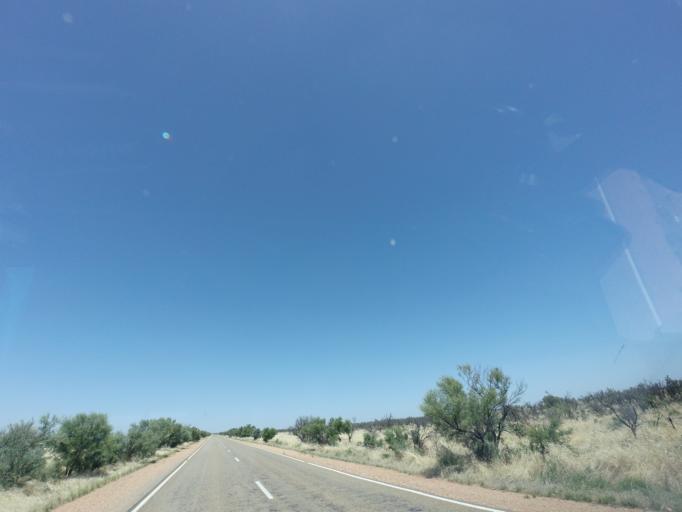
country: AU
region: South Australia
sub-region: Flinders Ranges
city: Quorn
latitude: -32.6675
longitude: 138.2340
